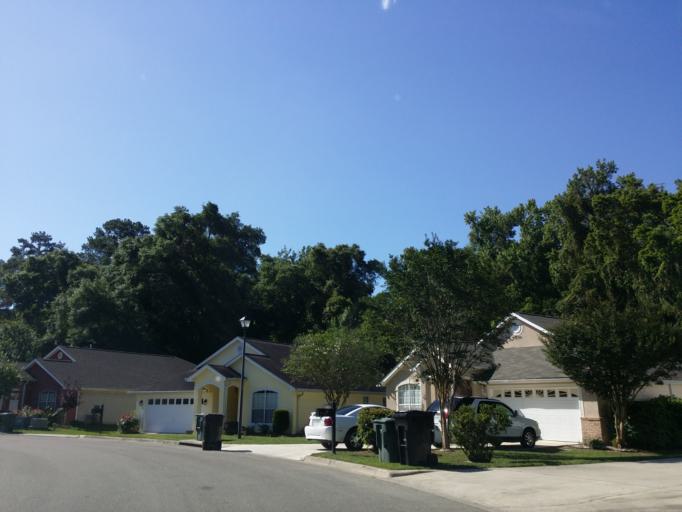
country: US
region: Florida
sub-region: Leon County
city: Tallahassee
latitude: 30.4564
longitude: -84.2209
